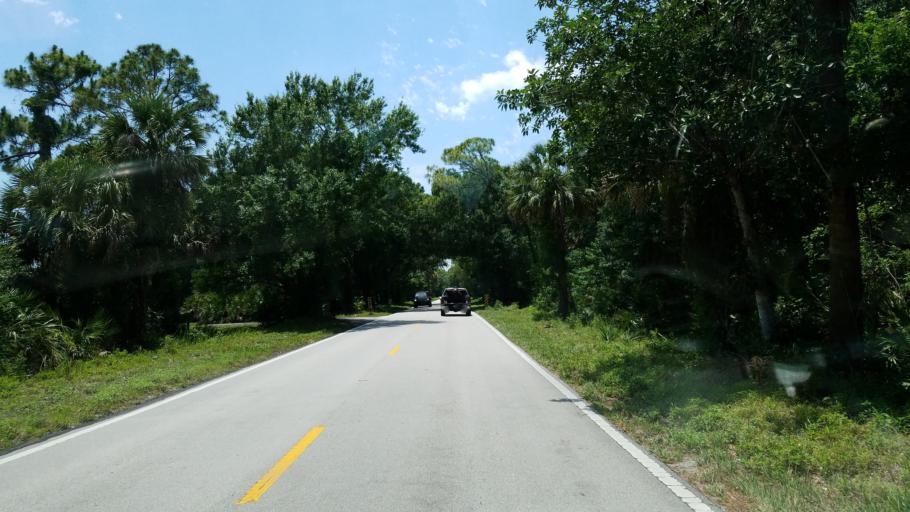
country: US
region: Florida
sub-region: Martin County
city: Indiantown
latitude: 27.1622
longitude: -80.5887
